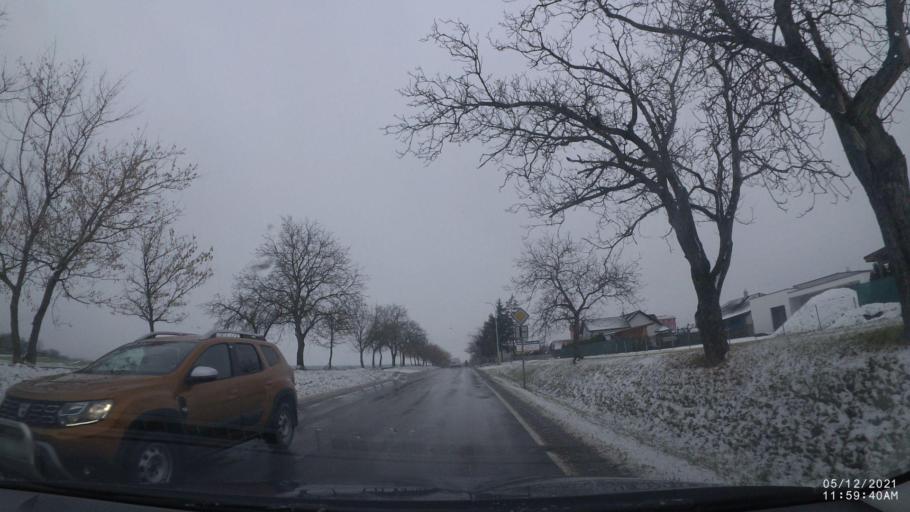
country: CZ
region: Kralovehradecky
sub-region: Okres Rychnov nad Kneznou
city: Opocno
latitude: 50.2744
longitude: 16.0980
